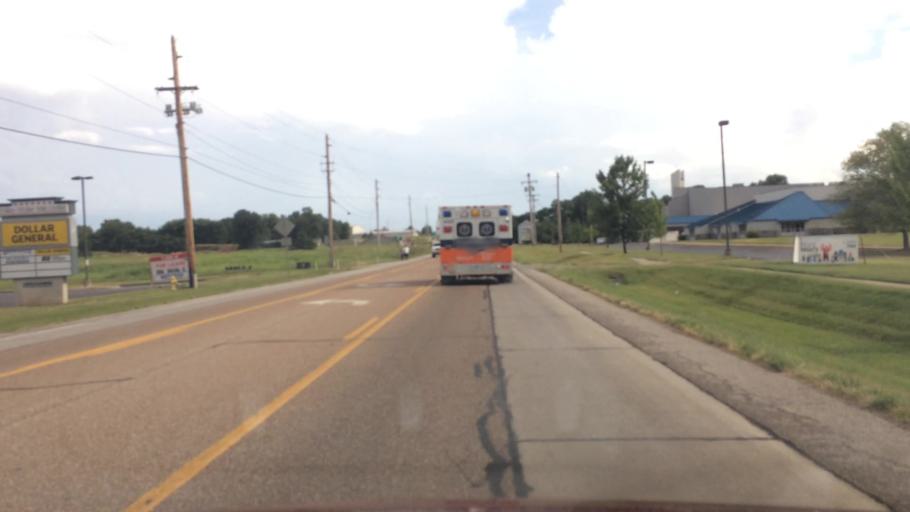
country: US
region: Missouri
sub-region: Greene County
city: Springfield
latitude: 37.2615
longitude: -93.2649
